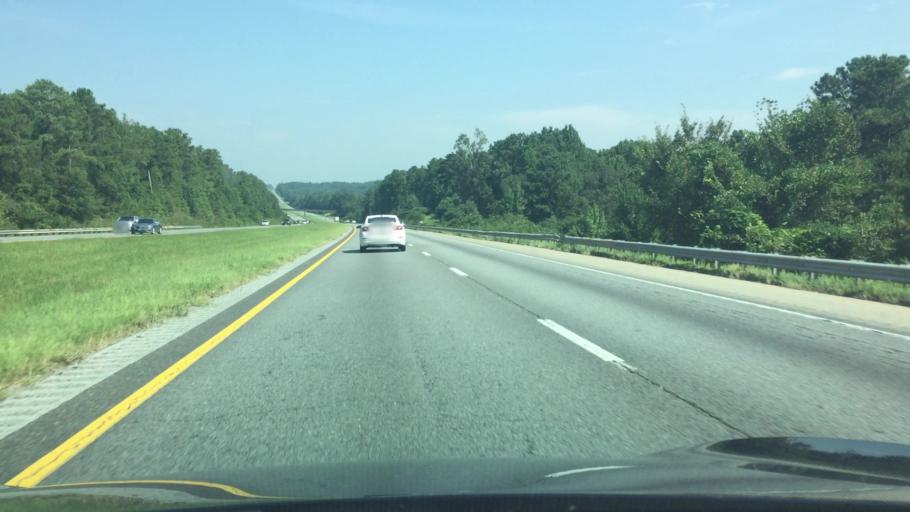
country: US
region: Alabama
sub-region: Autauga County
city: Marbury
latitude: 32.6483
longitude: -86.4960
